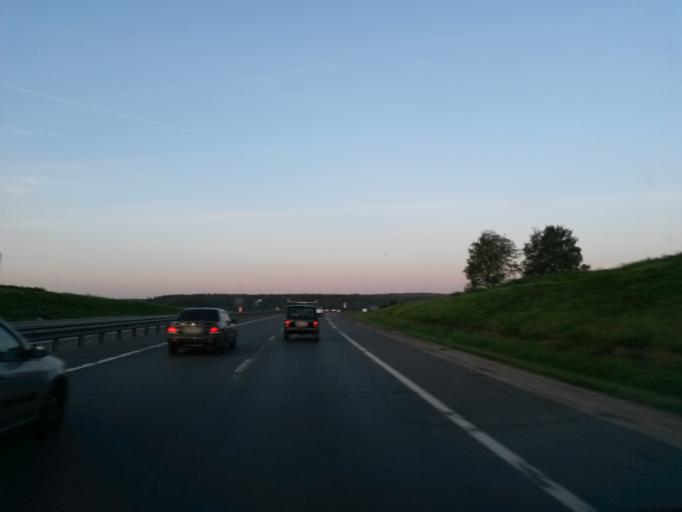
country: RU
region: Moskovskaya
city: Sergiyev Posad
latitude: 56.2726
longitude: 38.1971
